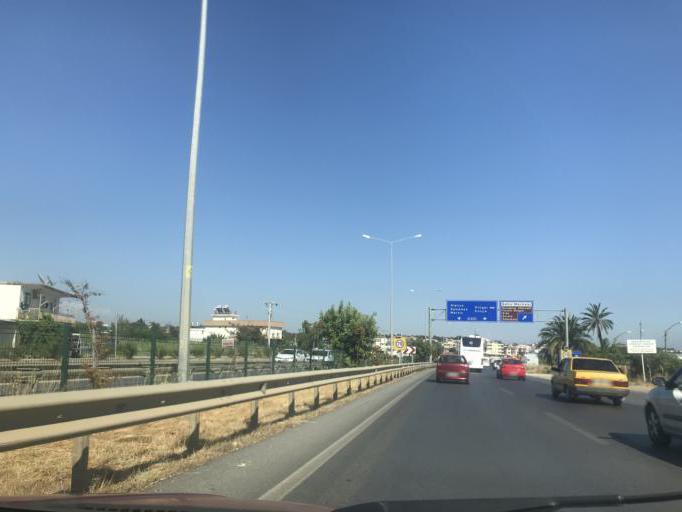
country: TR
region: Antalya
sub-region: Manavgat
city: Side
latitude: 36.7990
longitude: 31.4049
